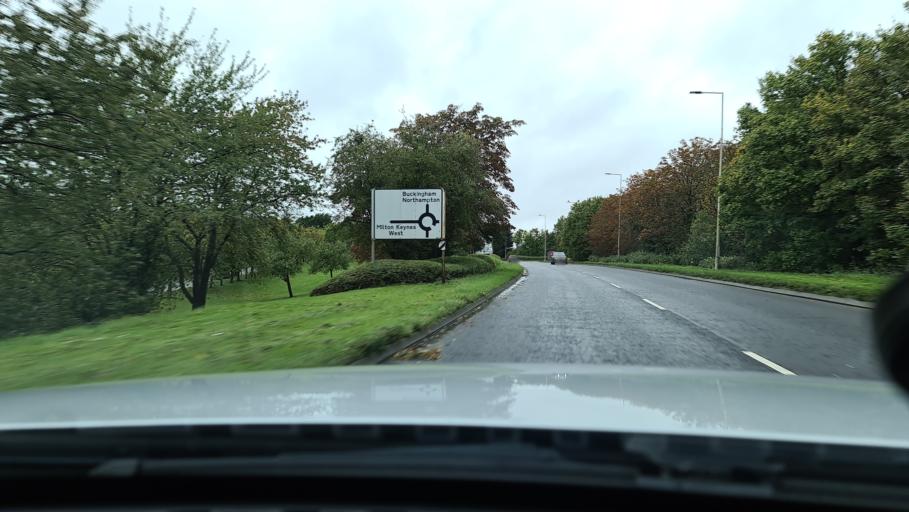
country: GB
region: England
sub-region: Milton Keynes
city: Bradwell
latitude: 52.0514
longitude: -0.8082
